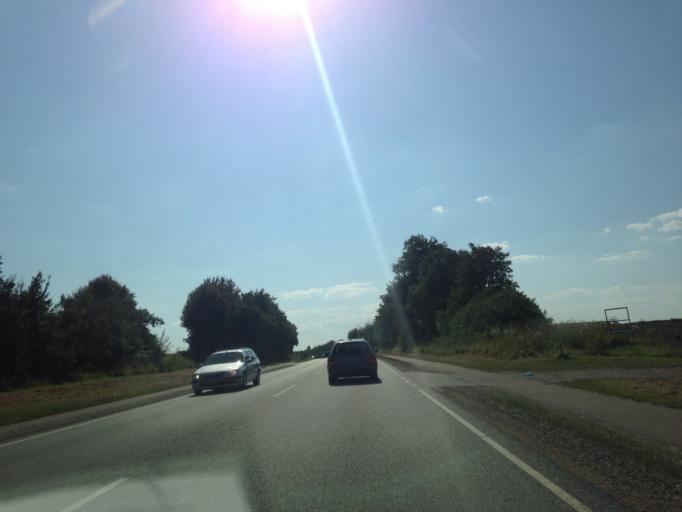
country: DK
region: Zealand
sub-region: Ringsted Kommune
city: Ringsted
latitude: 55.4776
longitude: 11.8355
